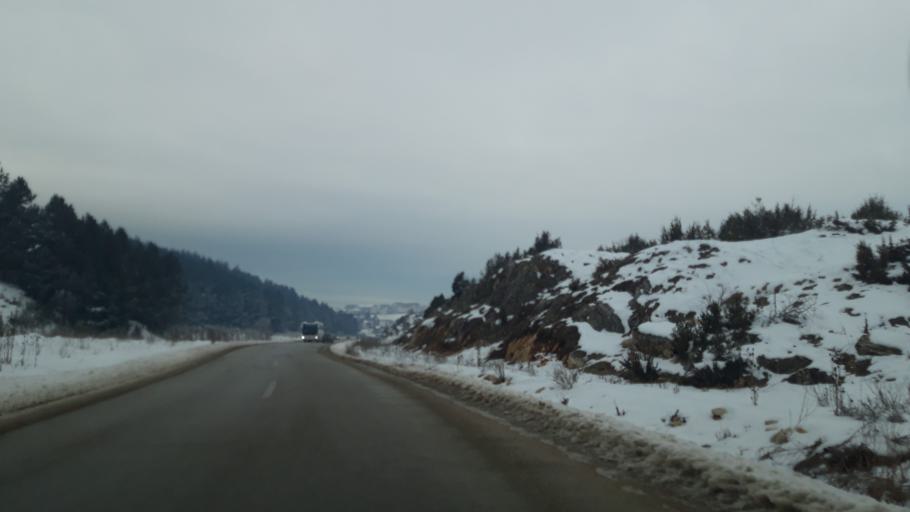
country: BA
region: Republika Srpska
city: Sokolac
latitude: 43.9364
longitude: 18.8129
